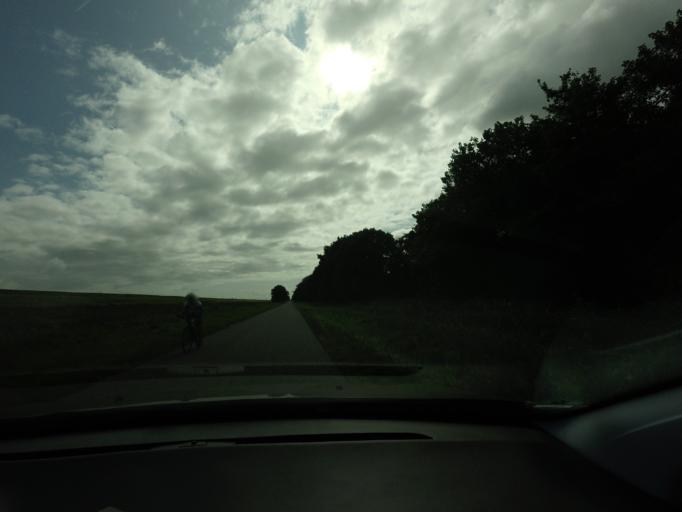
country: NL
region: North Holland
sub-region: Gemeente Hollands Kroon
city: Den Oever
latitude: 52.8866
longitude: 5.0783
